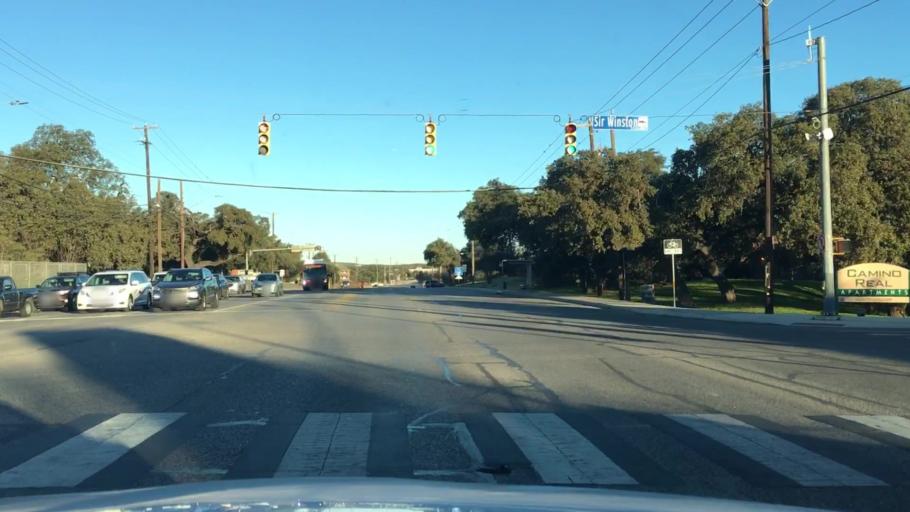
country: US
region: Texas
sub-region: Bexar County
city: Castle Hills
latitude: 29.5516
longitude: -98.5125
